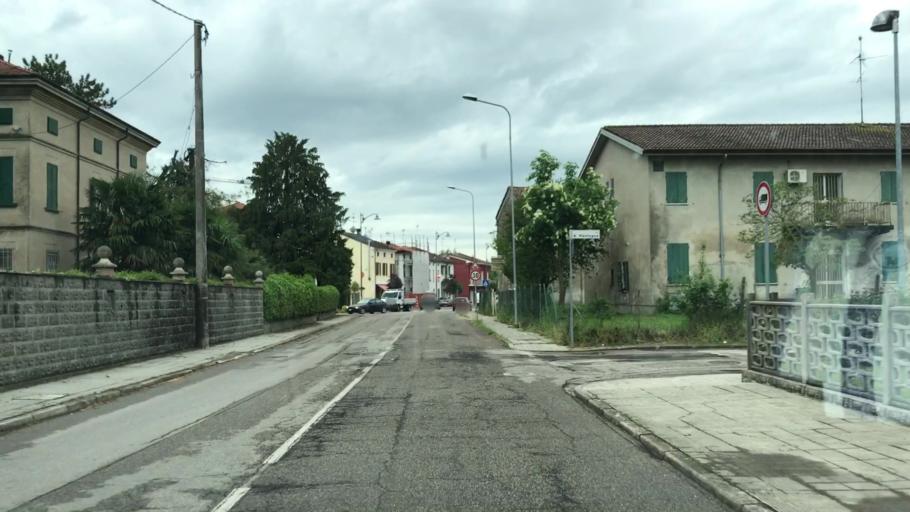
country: IT
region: Lombardy
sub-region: Provincia di Mantova
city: San Giovanni del Dosso
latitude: 44.9693
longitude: 11.0824
